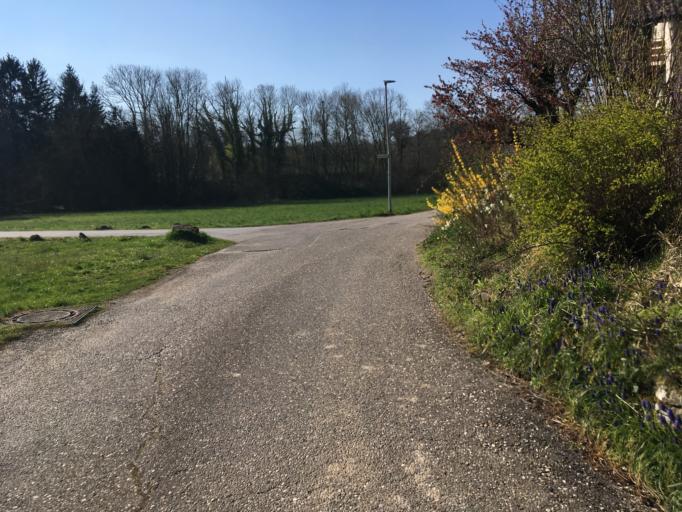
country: DE
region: Baden-Wuerttemberg
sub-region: Regierungsbezirk Stuttgart
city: Talheim
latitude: 49.0967
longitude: 9.1798
